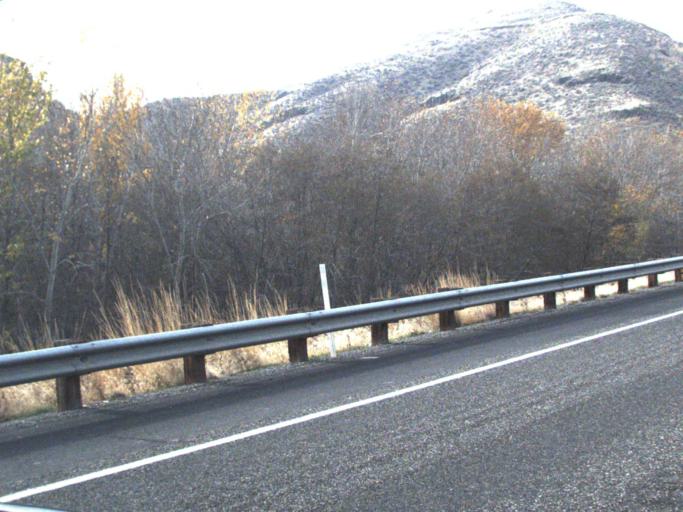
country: US
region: Washington
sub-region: Asotin County
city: Clarkston Heights-Vineland
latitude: 46.4045
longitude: -117.2513
